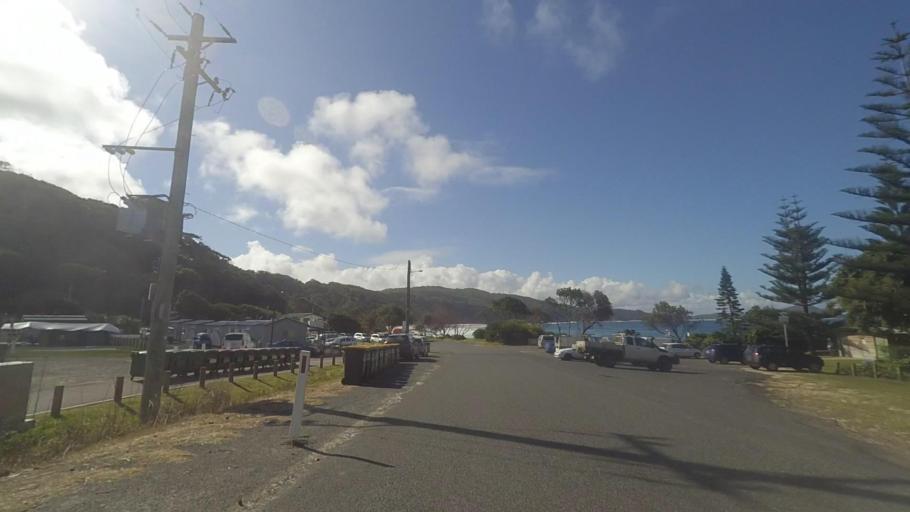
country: AU
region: New South Wales
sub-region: Great Lakes
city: Forster
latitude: -32.4331
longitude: 152.5245
